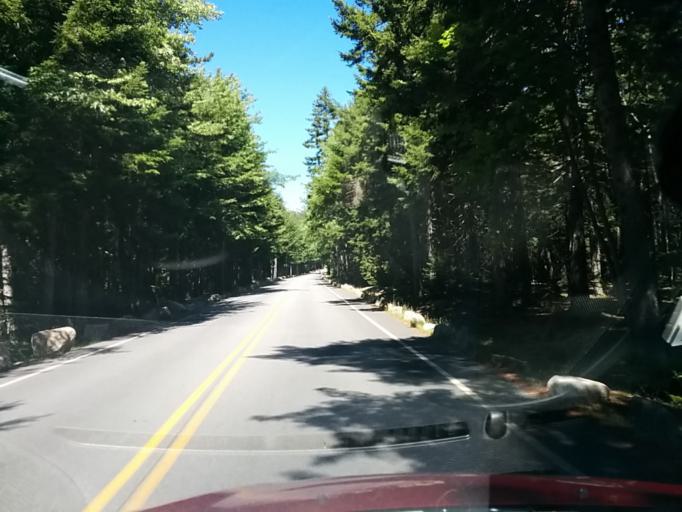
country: US
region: Maine
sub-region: Hancock County
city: Bar Harbor
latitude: 44.3151
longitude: -68.2491
